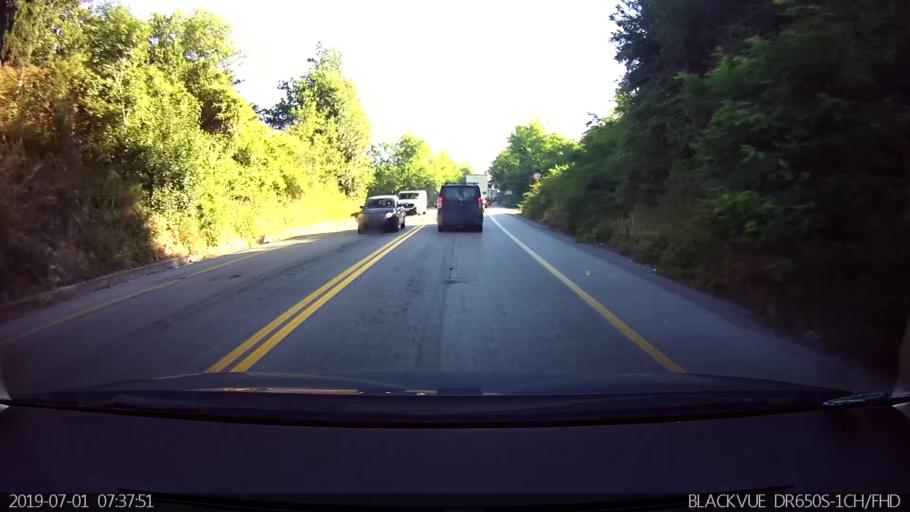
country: IT
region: Latium
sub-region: Provincia di Frosinone
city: Giuliano di Roma
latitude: 41.5406
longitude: 13.2674
